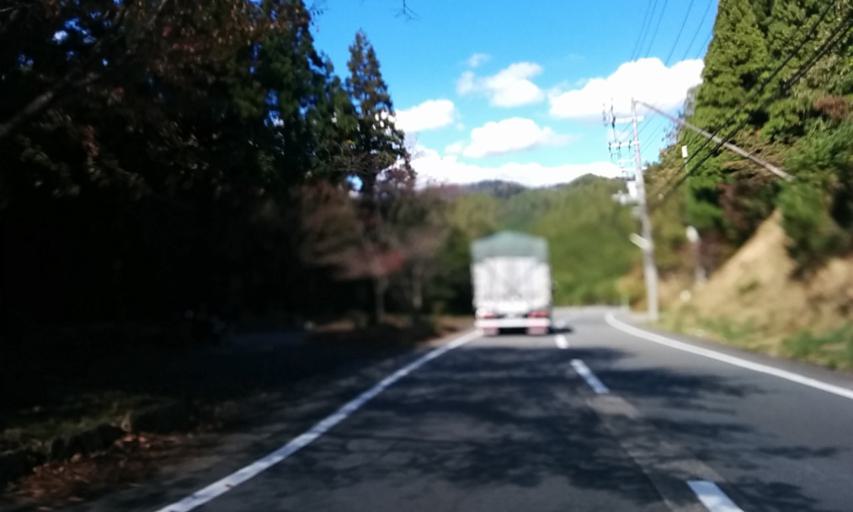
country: JP
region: Kyoto
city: Kameoka
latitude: 35.2010
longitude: 135.6168
